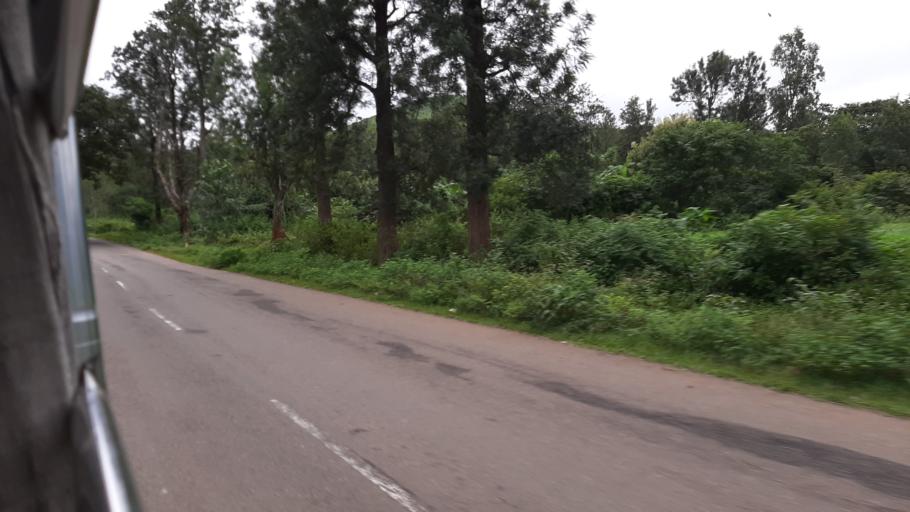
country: IN
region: Andhra Pradesh
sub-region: Vizianagaram District
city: Salur
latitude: 18.2878
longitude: 82.9324
